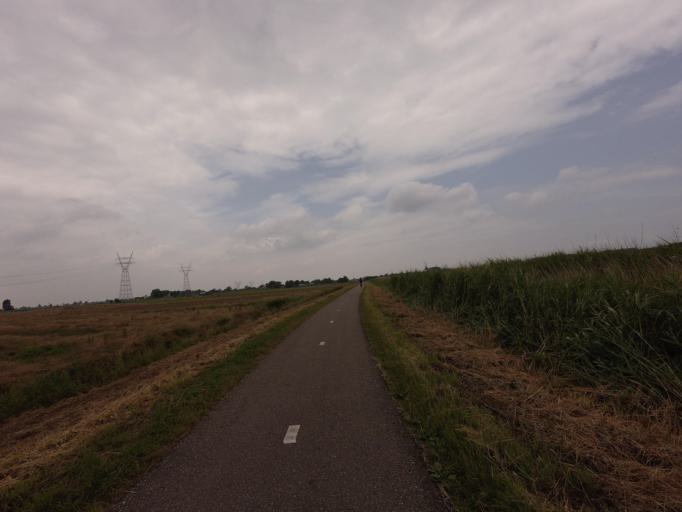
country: NL
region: North Holland
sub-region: Gemeente Purmerend
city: Purmerend
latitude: 52.4739
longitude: 4.9545
